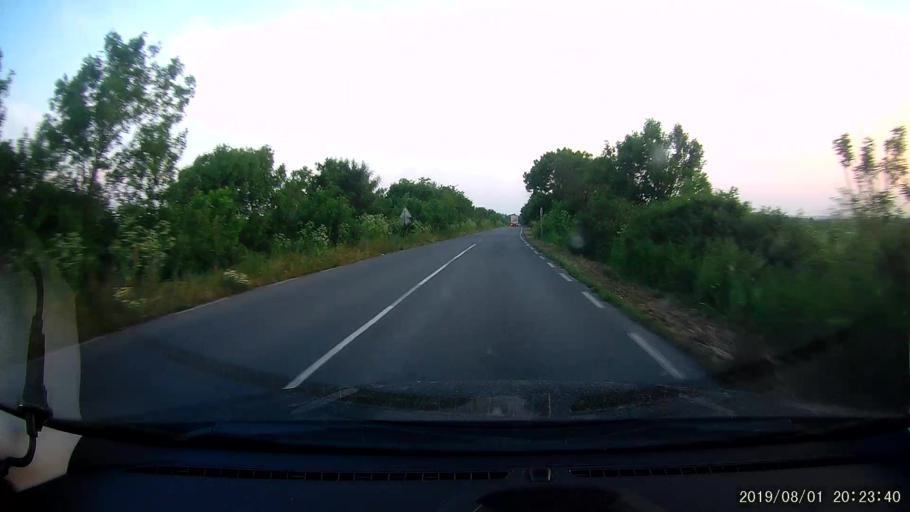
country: BG
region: Yambol
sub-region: Obshtina Elkhovo
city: Elkhovo
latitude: 42.2444
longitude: 26.5987
